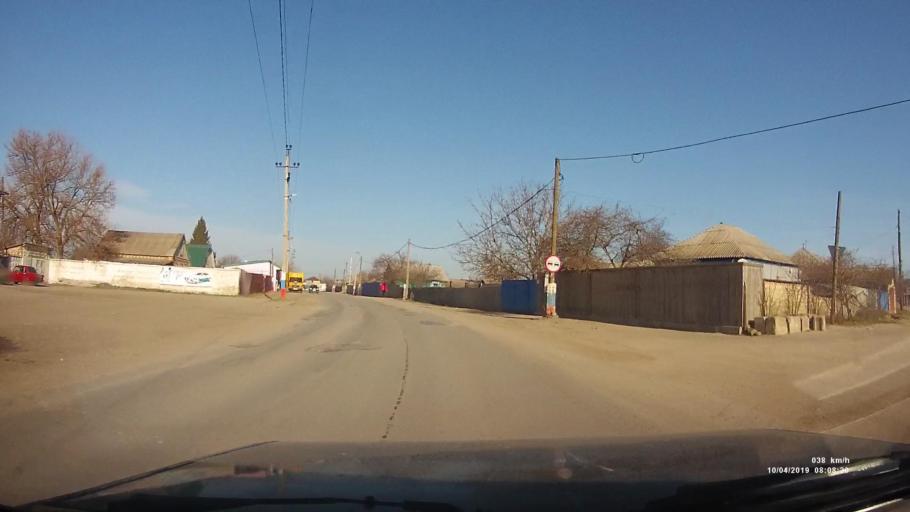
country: RU
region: Rostov
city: Staraya Stanitsa
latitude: 48.3478
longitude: 40.2862
